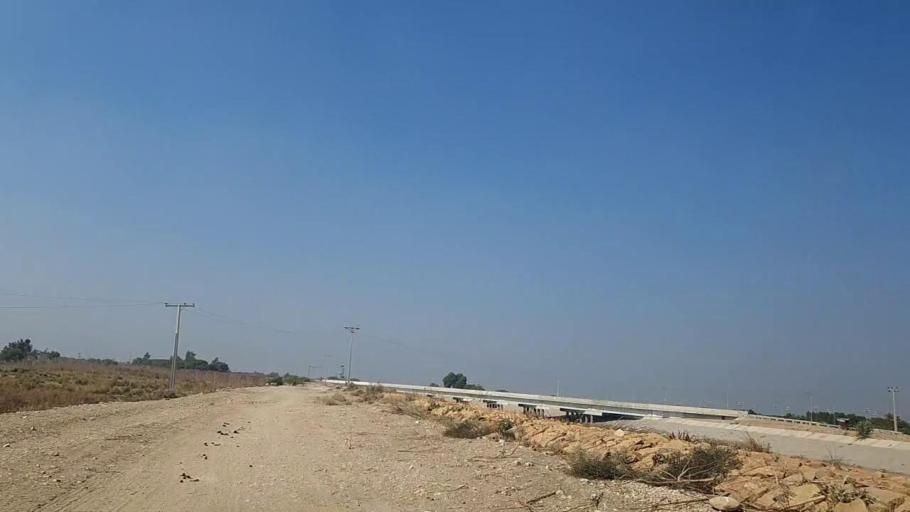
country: PK
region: Sindh
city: Sakrand
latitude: 26.2434
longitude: 68.2662
